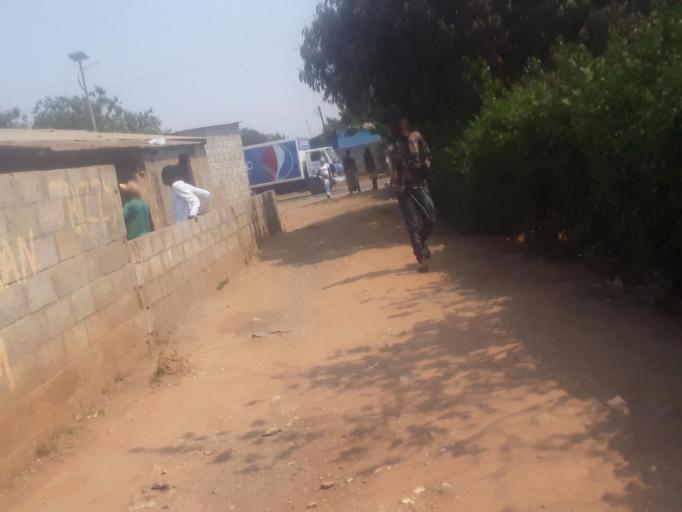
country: ZM
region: Lusaka
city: Lusaka
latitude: -15.3529
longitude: 28.2854
